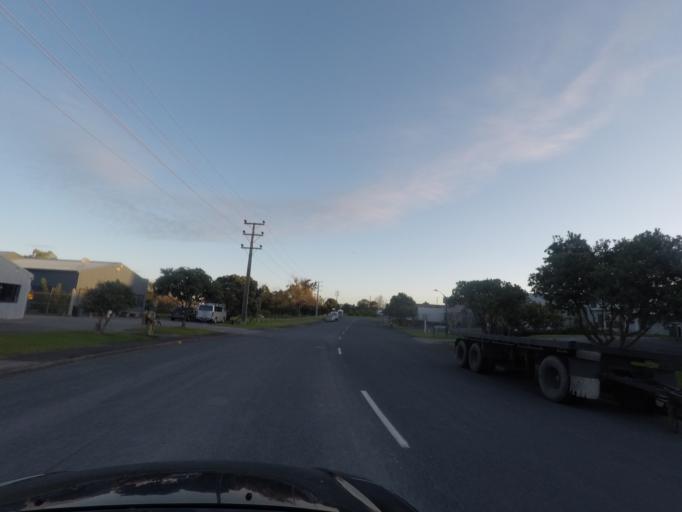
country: NZ
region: Auckland
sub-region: Auckland
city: Rosebank
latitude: -36.8905
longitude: 174.6616
